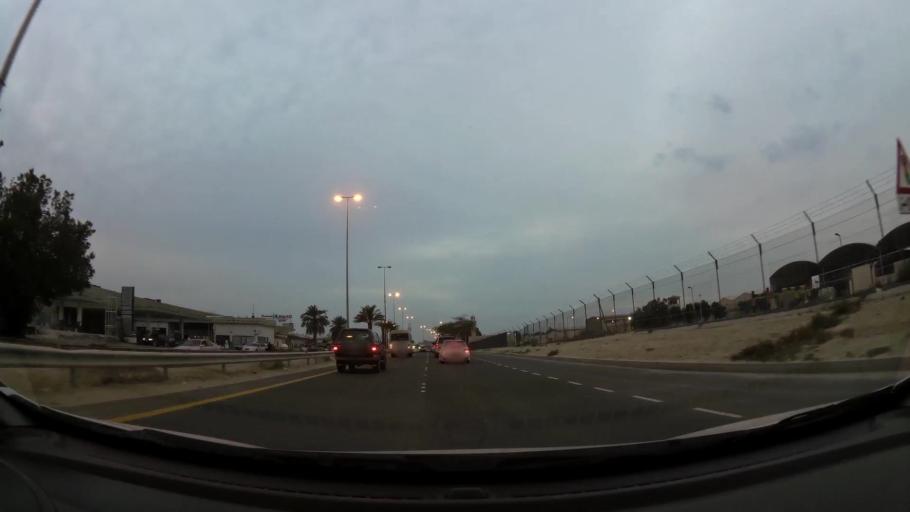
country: BH
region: Northern
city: Ar Rifa'
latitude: 26.1121
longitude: 50.5761
